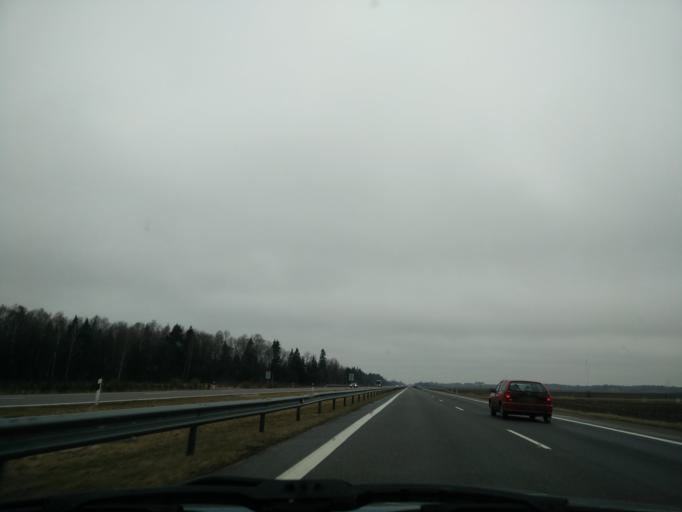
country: LT
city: Raseiniai
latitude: 55.3749
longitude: 22.9461
